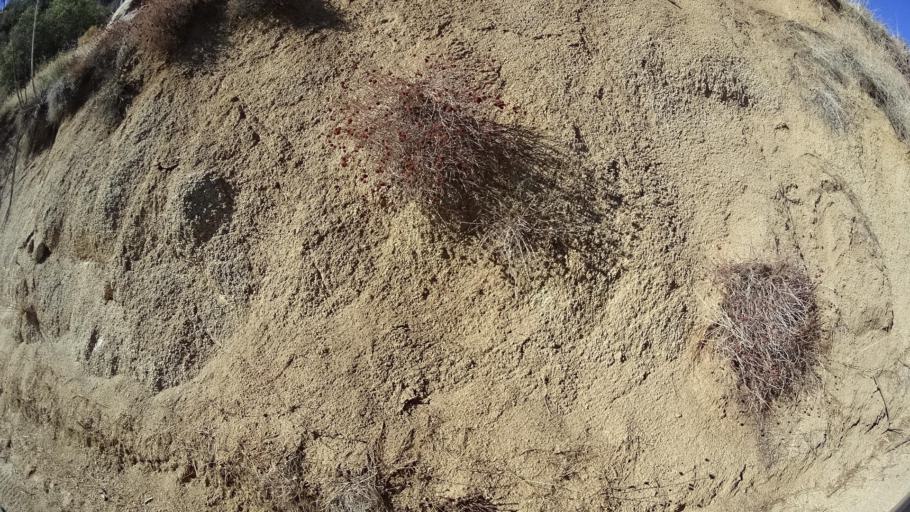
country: US
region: California
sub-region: Kern County
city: Wofford Heights
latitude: 35.7041
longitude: -118.4883
